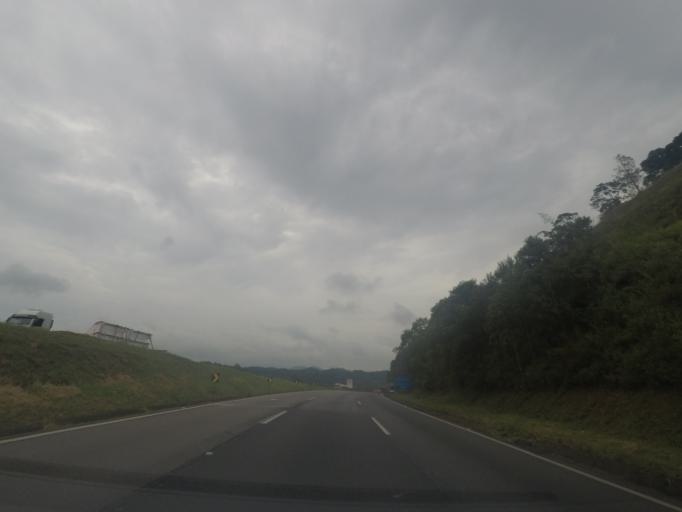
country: BR
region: Sao Paulo
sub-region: Cajati
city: Cajati
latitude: -24.9127
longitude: -48.2534
